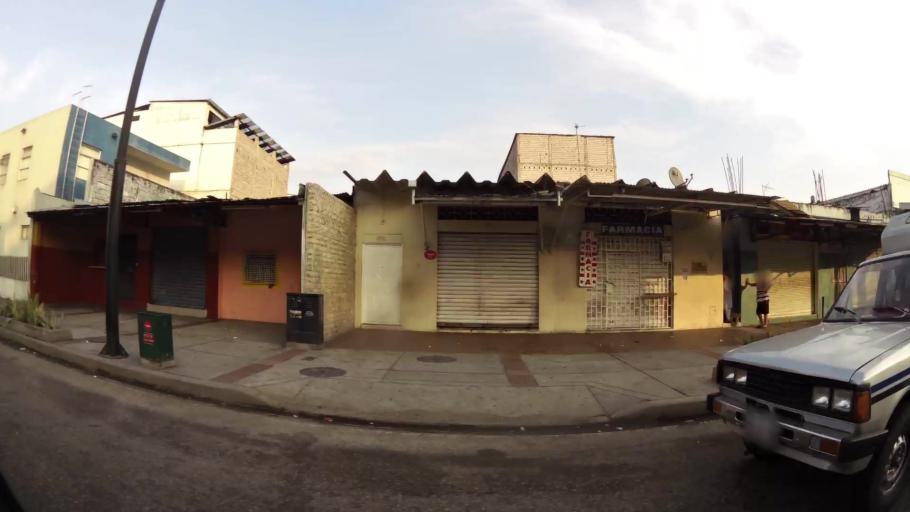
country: EC
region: Guayas
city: Guayaquil
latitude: -2.1952
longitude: -79.8963
